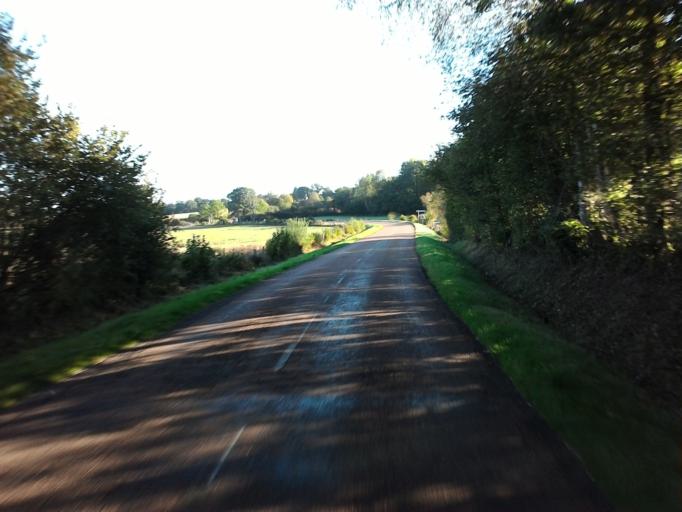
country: FR
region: Bourgogne
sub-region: Departement de la Cote-d'Or
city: Saulieu
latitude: 47.2814
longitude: 4.1398
